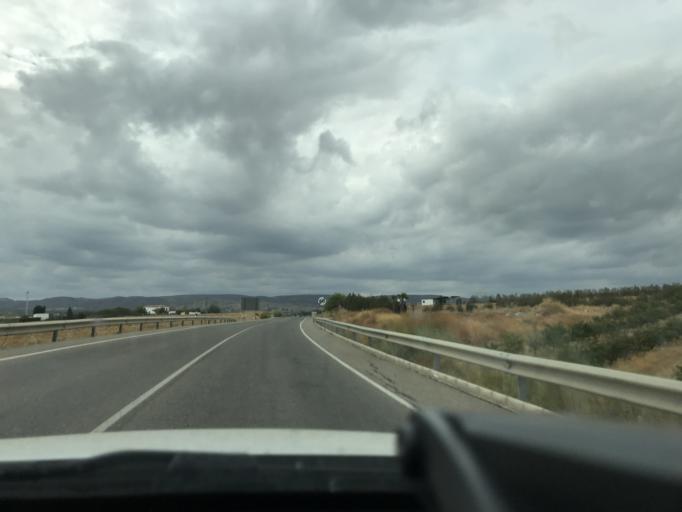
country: ES
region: Andalusia
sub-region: Provincia de Sevilla
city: Cantillana
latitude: 37.6163
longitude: -5.8101
